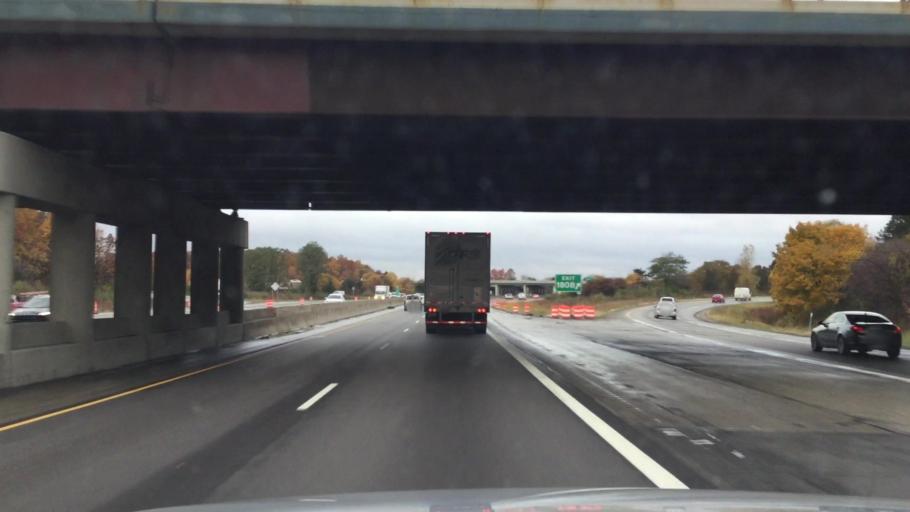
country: US
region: Michigan
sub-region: Washtenaw County
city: Ypsilanti
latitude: 42.2249
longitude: -83.6798
